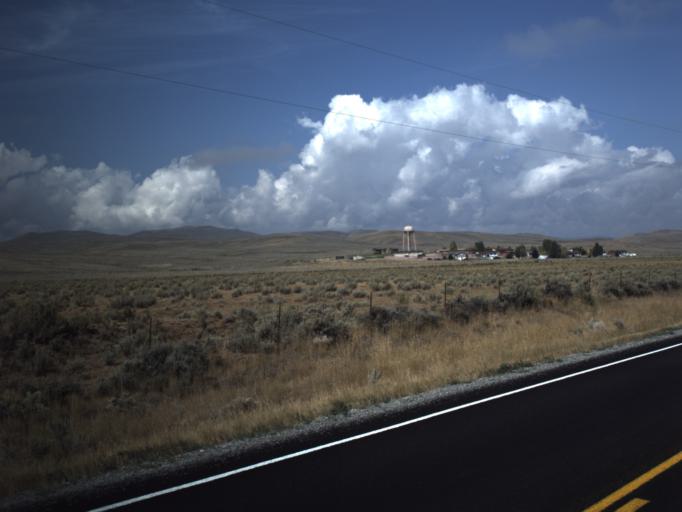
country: US
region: Utah
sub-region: Rich County
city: Randolph
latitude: 41.5816
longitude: -111.1661
